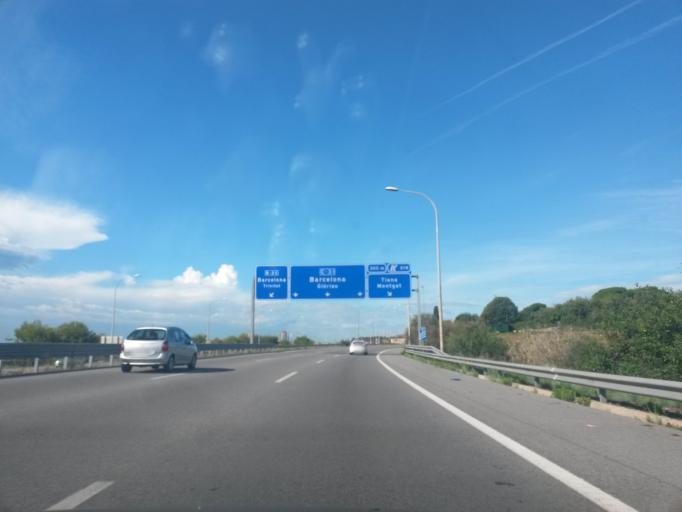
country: ES
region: Catalonia
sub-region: Provincia de Barcelona
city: Alella
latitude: 41.4808
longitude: 2.2925
